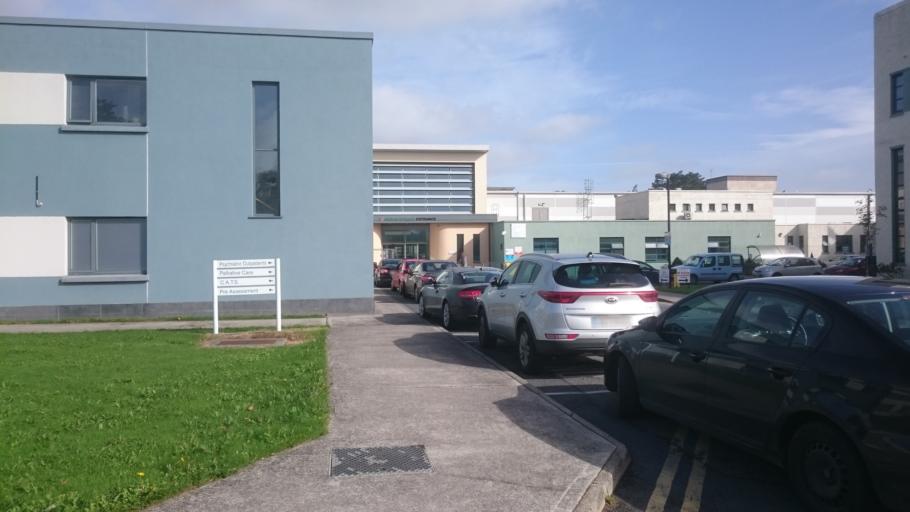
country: IE
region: Leinster
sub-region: Kilkenny
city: Kilkenny
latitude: 52.6658
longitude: -7.2639
